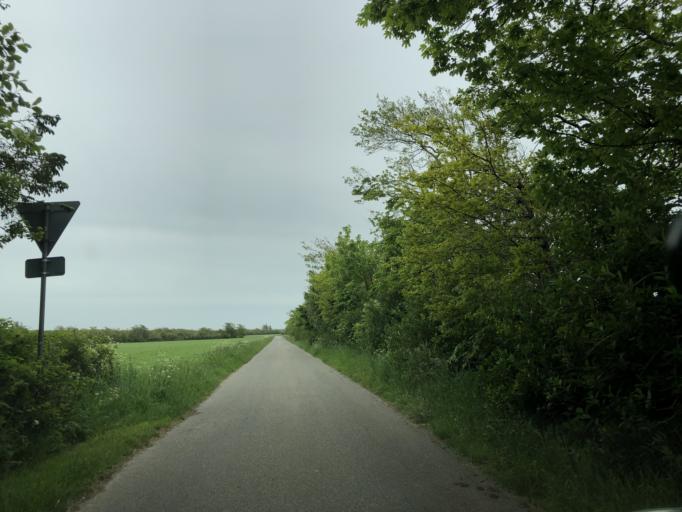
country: DK
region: Central Jutland
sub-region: Holstebro Kommune
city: Ulfborg
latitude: 56.2773
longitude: 8.1754
